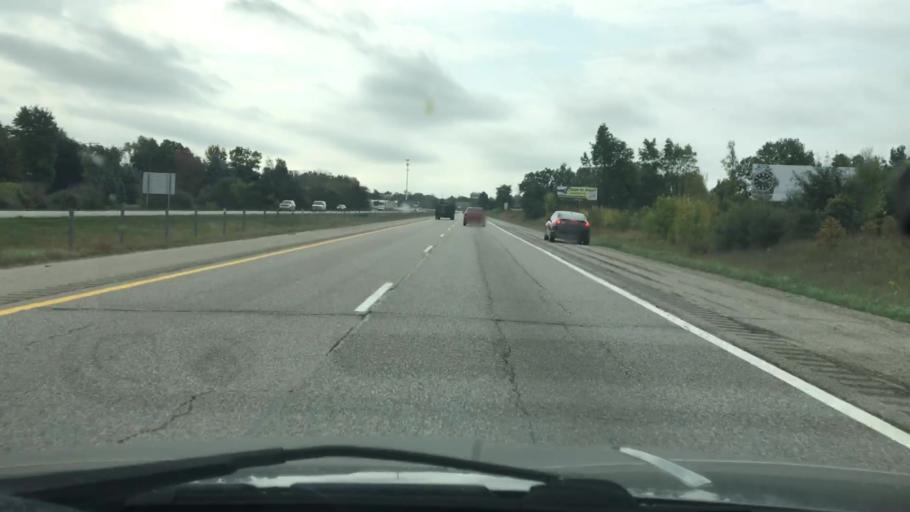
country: US
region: Michigan
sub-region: Livingston County
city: Brighton
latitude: 42.6256
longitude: -83.7489
